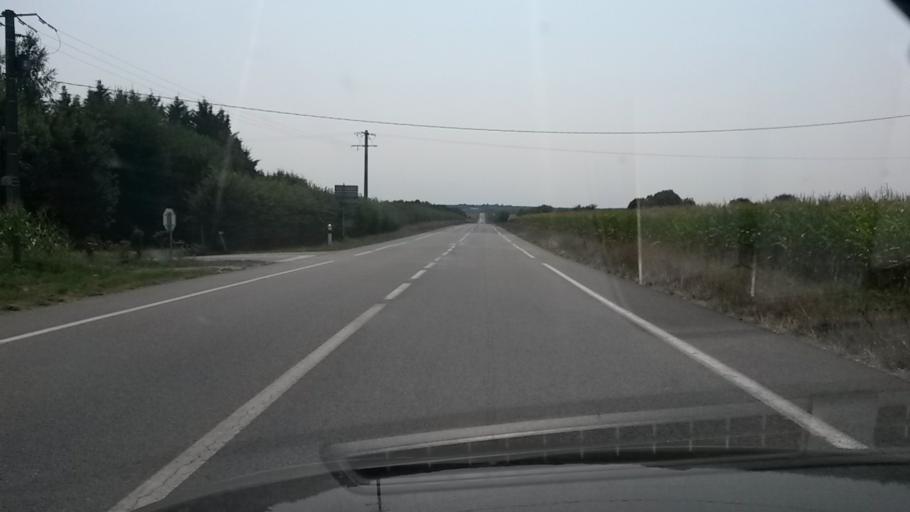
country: FR
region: Pays de la Loire
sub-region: Departement de la Mayenne
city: Chemaze
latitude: 47.7763
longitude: -0.7792
